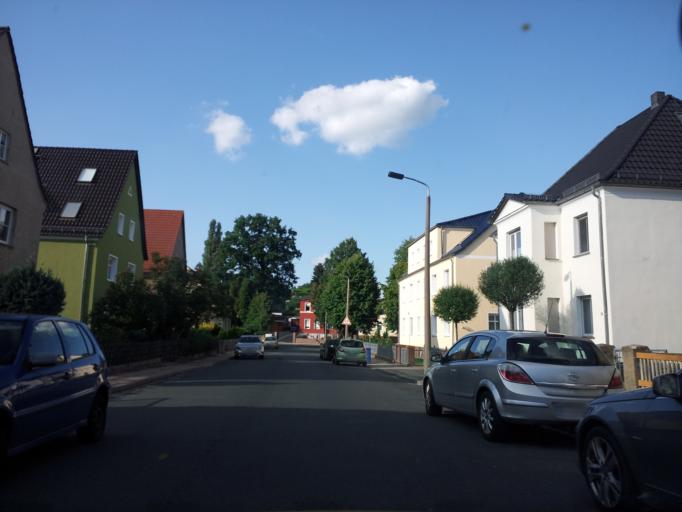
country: DE
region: Brandenburg
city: Juterbog
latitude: 51.9990
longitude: 13.0807
